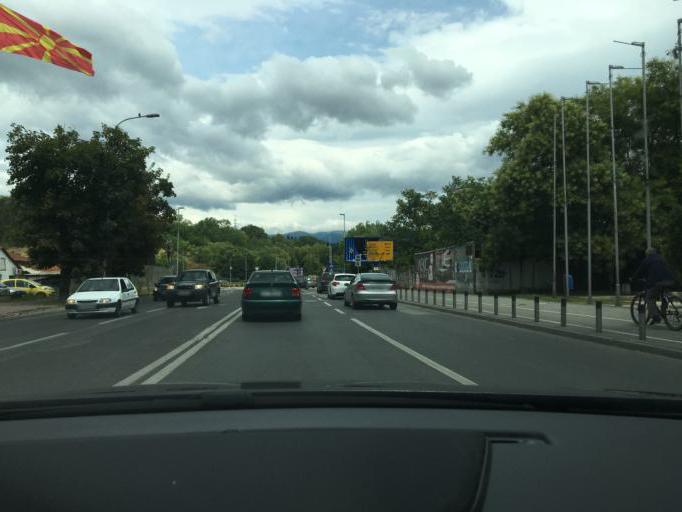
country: MK
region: Karpos
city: Skopje
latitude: 41.9977
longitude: 21.4504
